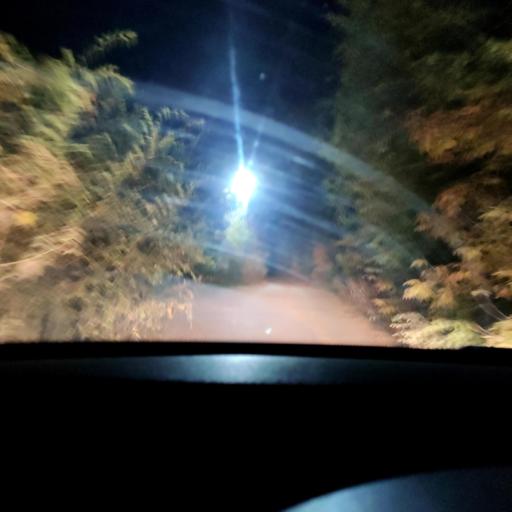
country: RU
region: Samara
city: Samara
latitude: 53.1699
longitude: 50.1843
